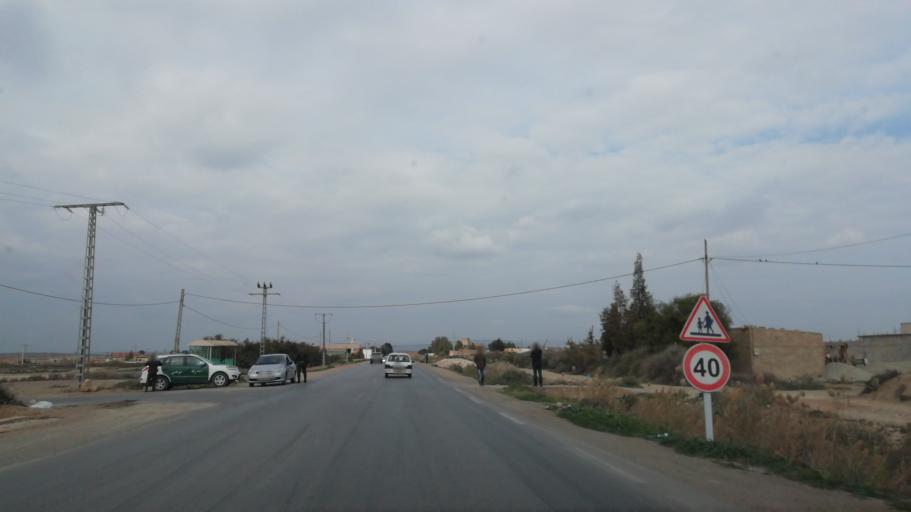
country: DZ
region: Mostaganem
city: Mostaganem
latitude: 35.6939
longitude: 0.0558
